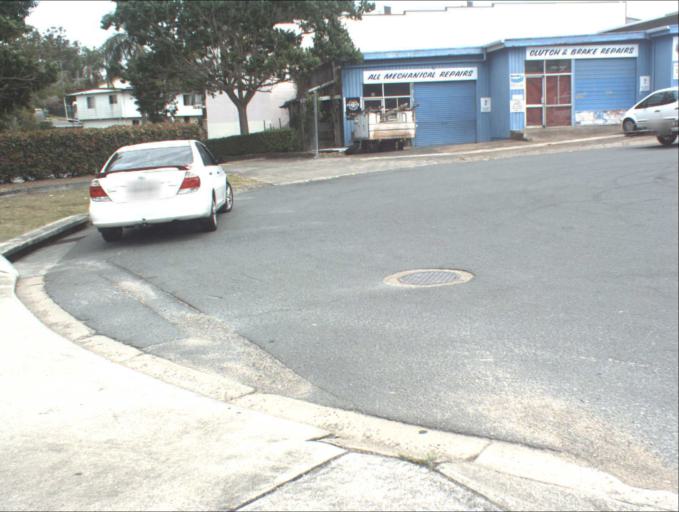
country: AU
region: Queensland
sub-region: Logan
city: Logan City
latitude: -27.6301
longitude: 153.1200
